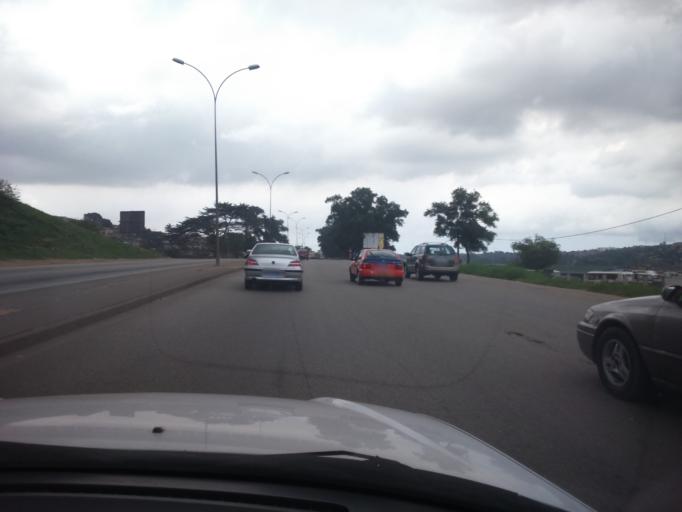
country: CI
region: Lagunes
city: Abidjan
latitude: 5.3563
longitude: -4.0402
